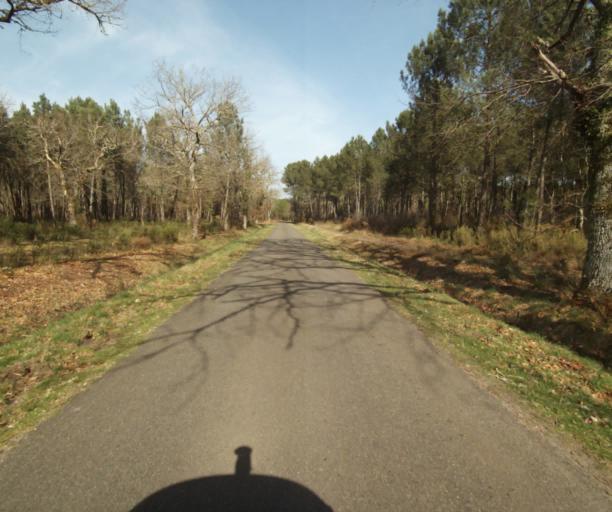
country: FR
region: Aquitaine
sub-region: Departement de la Gironde
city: Bazas
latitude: 44.2329
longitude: -0.2023
